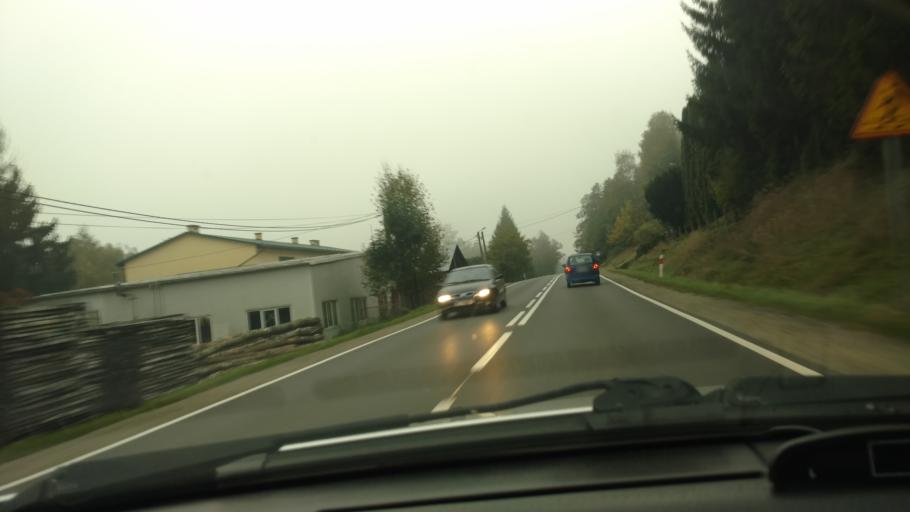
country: PL
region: Subcarpathian Voivodeship
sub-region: Powiat strzyzowski
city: Frysztak
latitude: 49.8359
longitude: 21.6121
